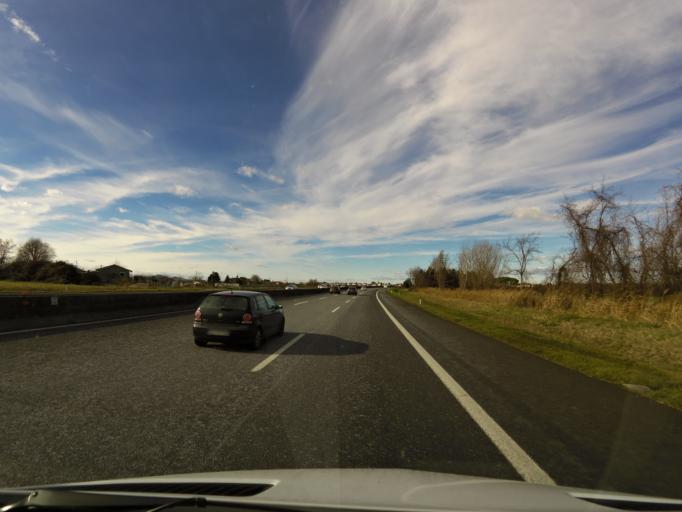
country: IT
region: Emilia-Romagna
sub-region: Forli-Cesena
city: Bagnarola
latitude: 44.1465
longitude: 12.3276
